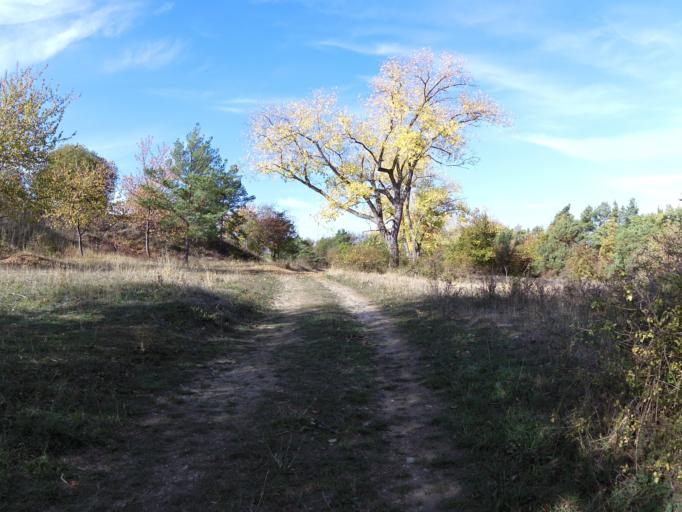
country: DE
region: Bavaria
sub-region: Regierungsbezirk Unterfranken
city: Eibelstadt
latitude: 49.7070
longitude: 9.9995
